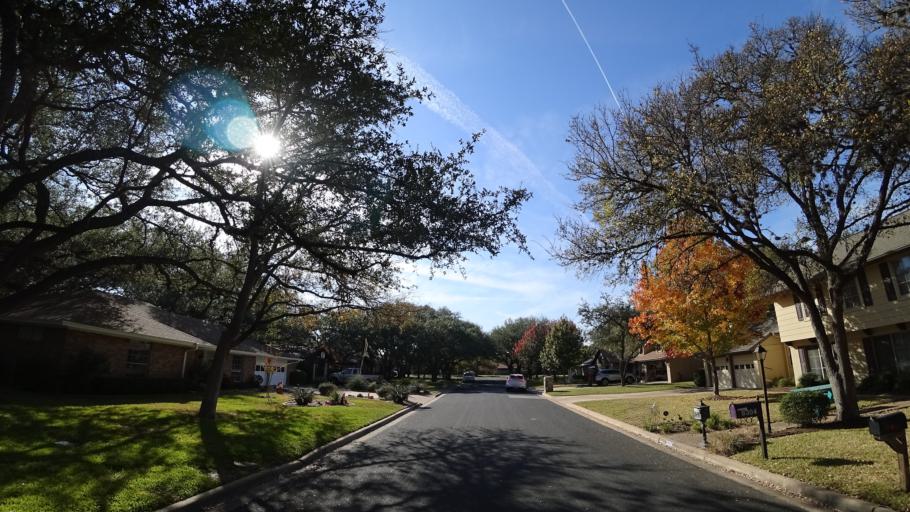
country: US
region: Texas
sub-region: Williamson County
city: Jollyville
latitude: 30.3766
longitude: -97.7563
